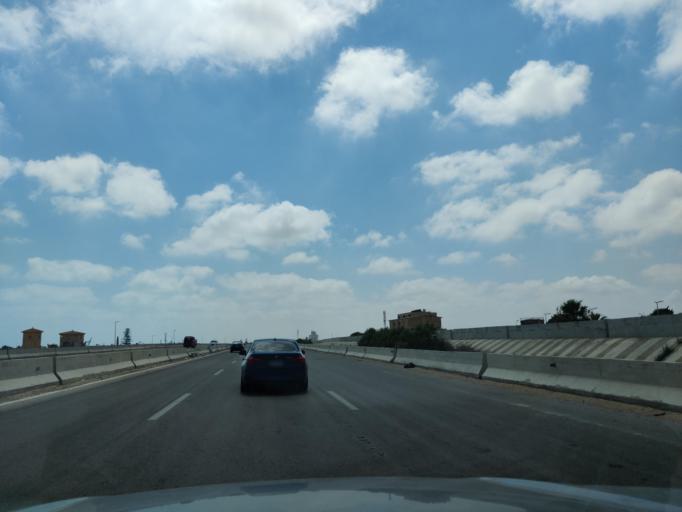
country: EG
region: Muhafazat Matruh
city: Al `Alamayn
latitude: 30.8207
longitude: 29.0144
